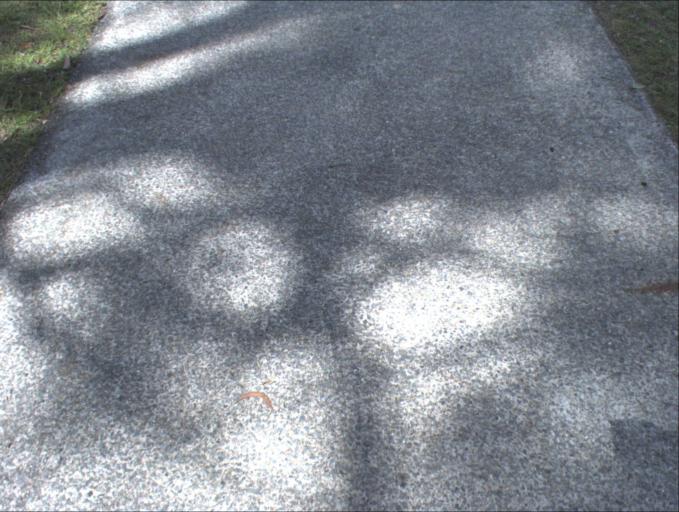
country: AU
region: Queensland
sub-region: Logan
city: Woodridge
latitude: -27.6681
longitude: 153.0597
